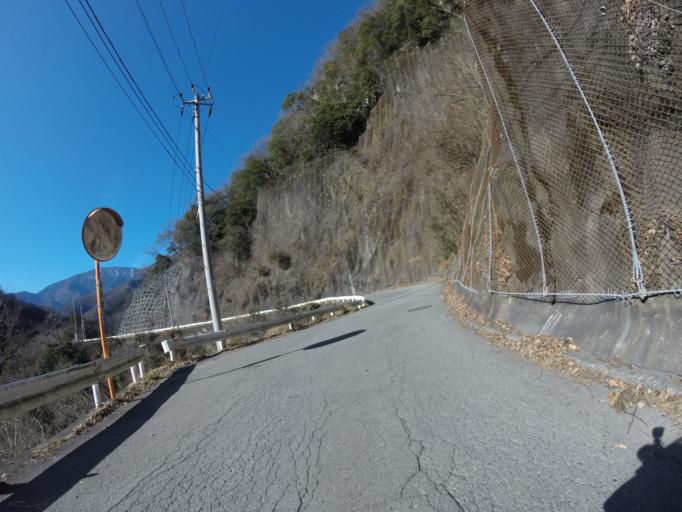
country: JP
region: Yamanashi
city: Ryuo
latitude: 35.4130
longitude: 138.3532
